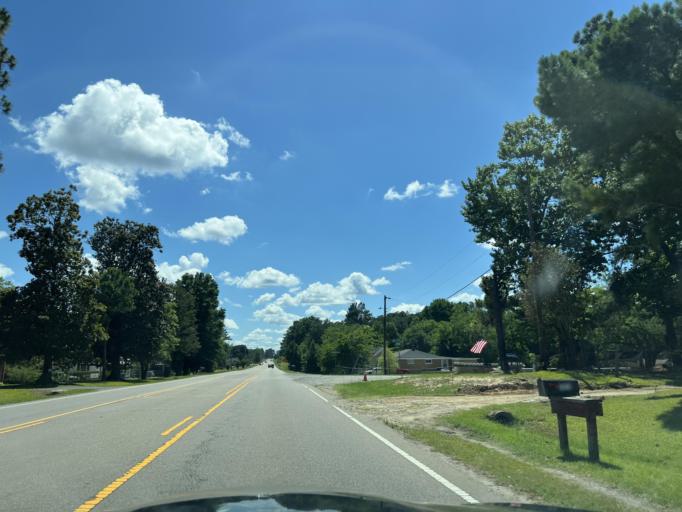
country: US
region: North Carolina
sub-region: Lee County
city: Sanford
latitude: 35.4425
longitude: -79.1788
